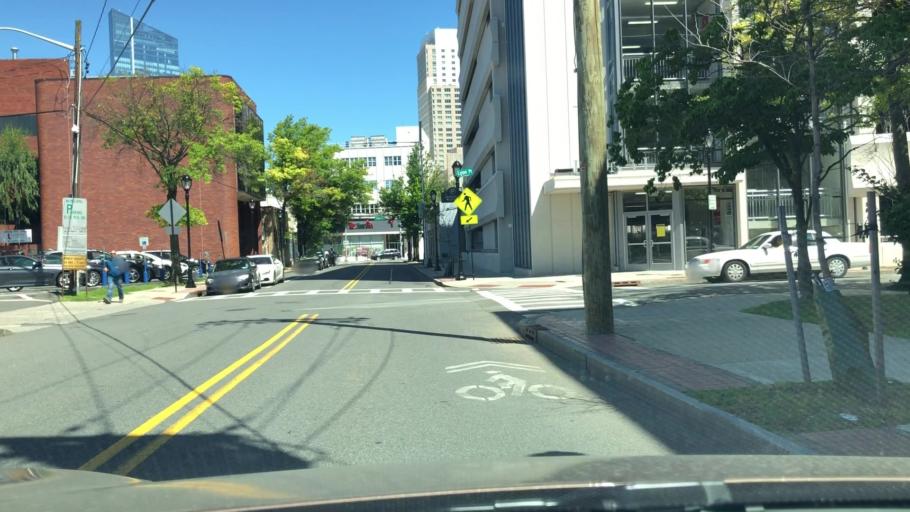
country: US
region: New York
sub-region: Westchester County
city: White Plains
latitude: 41.0288
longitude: -73.7637
